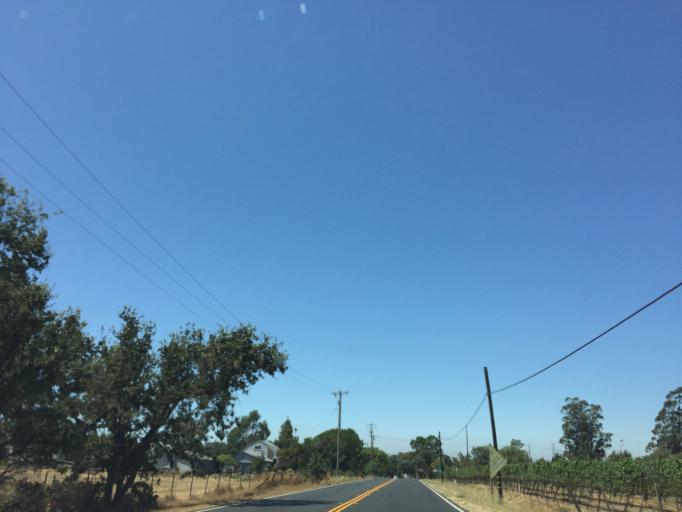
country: US
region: California
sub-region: Sonoma County
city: Sonoma
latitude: 38.2461
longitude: -122.4353
